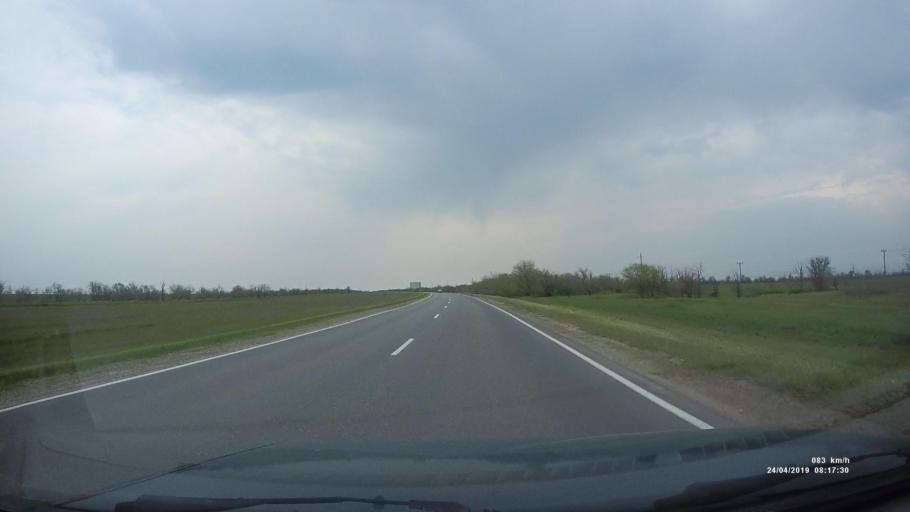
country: RU
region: Kalmykiya
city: Priyutnoye
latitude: 46.0979
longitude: 43.6311
